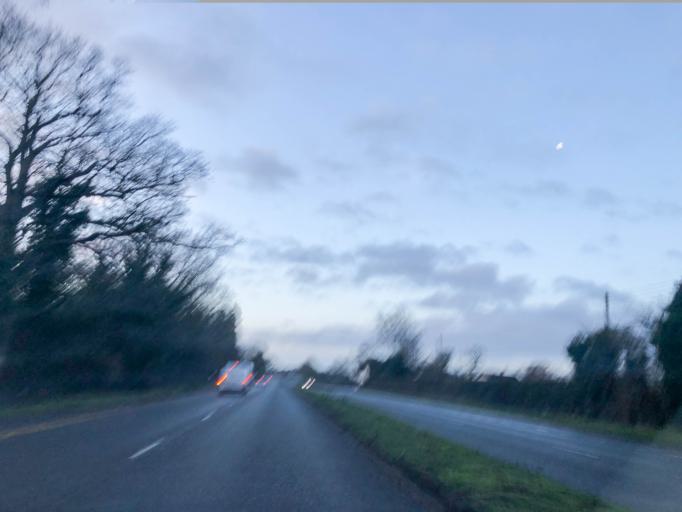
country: GB
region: England
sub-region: Solihull
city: Tidbury Green
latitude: 52.3699
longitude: -1.8870
